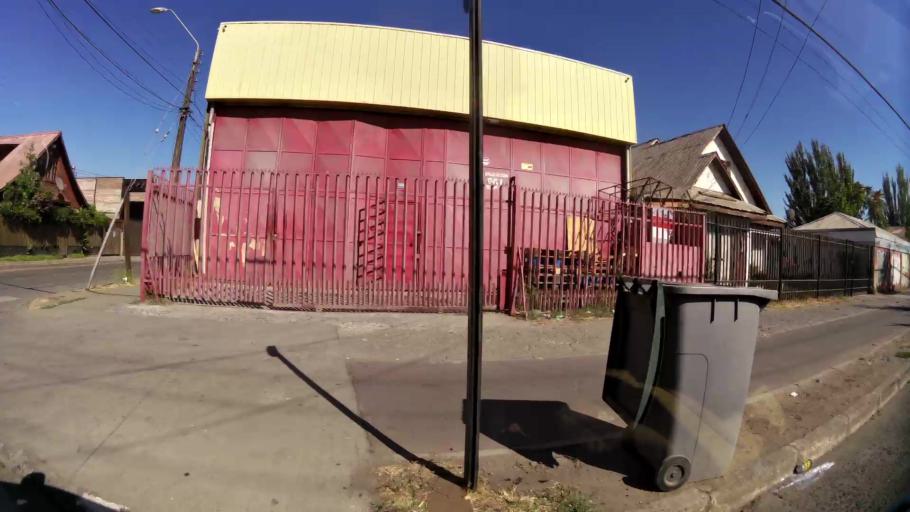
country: CL
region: Maule
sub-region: Provincia de Curico
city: Curico
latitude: -34.9826
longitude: -71.2493
